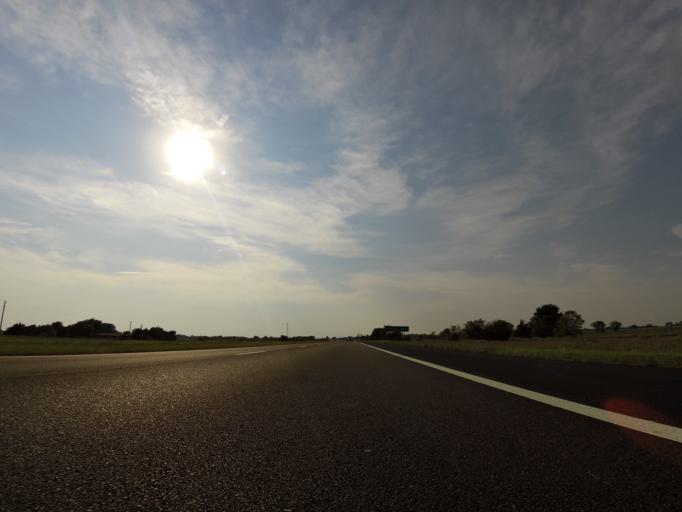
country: US
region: Kansas
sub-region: Reno County
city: Haven
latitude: 37.8909
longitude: -97.7538
